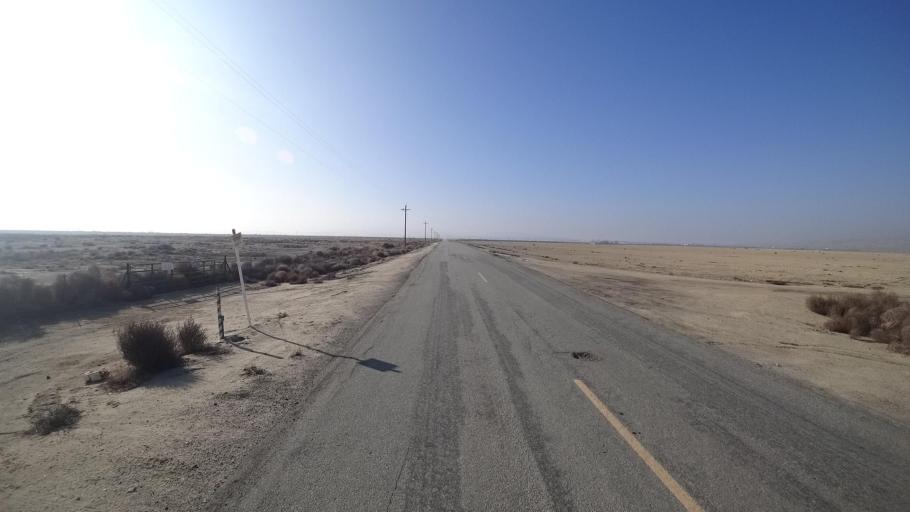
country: US
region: California
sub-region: Kern County
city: Maricopa
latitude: 35.1012
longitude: -119.3589
